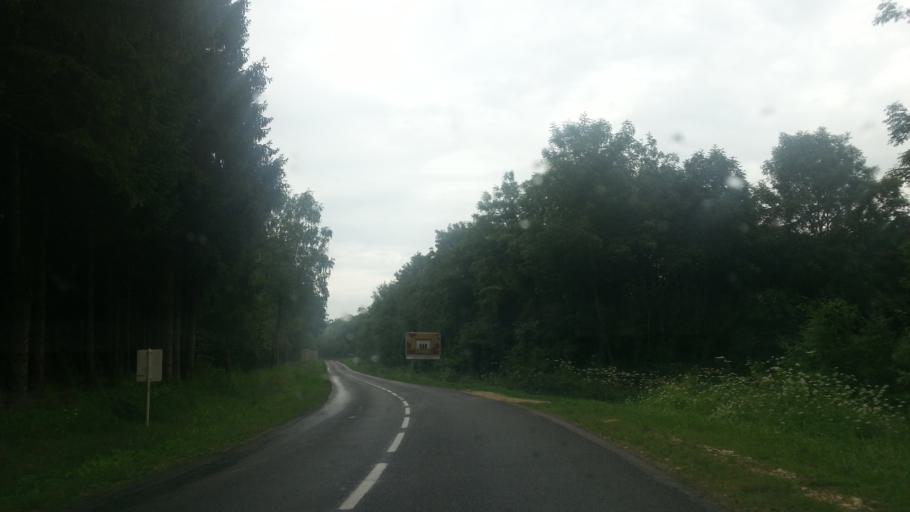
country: FR
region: Lorraine
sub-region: Departement de la Meuse
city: Verdun
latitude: 49.2015
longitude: 5.4238
